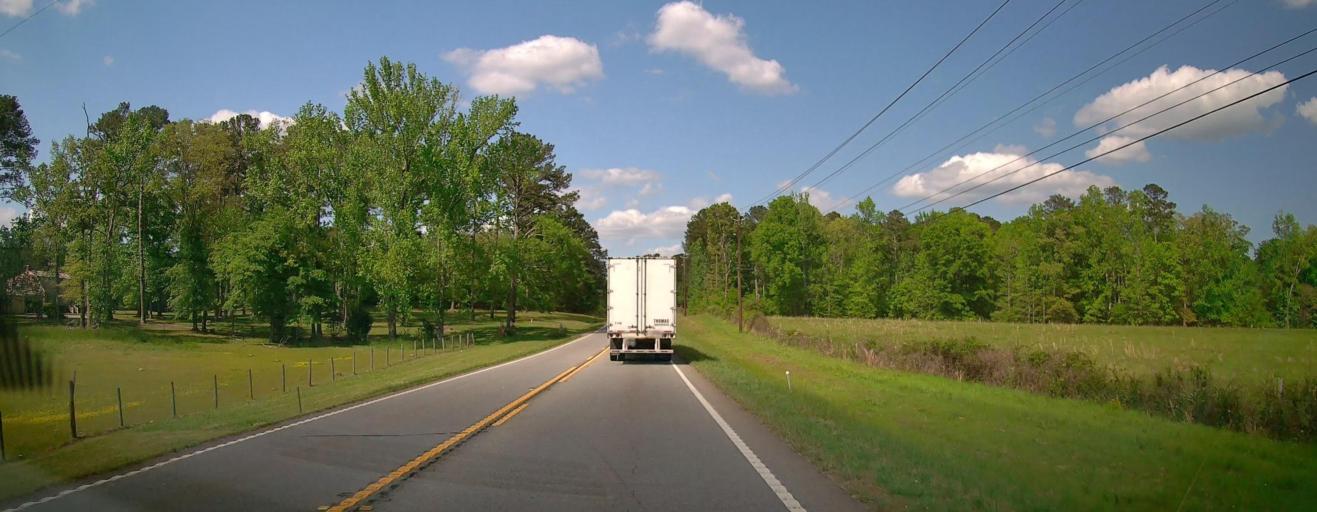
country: US
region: Georgia
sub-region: Greene County
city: Greensboro
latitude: 33.5161
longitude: -83.2250
